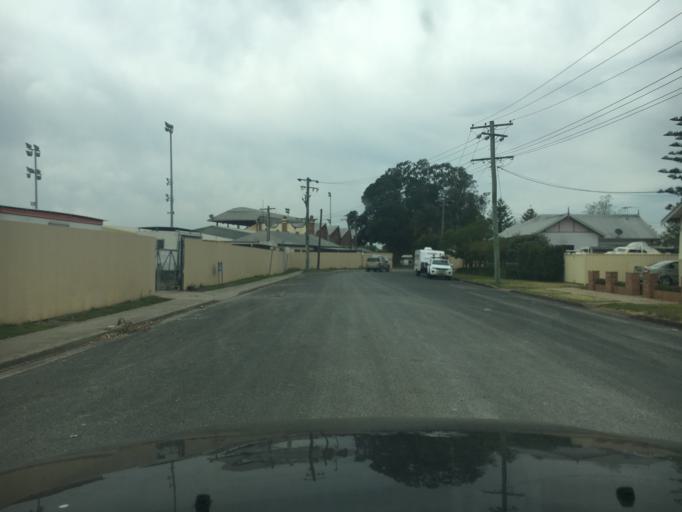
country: AU
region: New South Wales
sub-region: Maitland Municipality
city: Maitland
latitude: -32.7439
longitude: 151.5607
